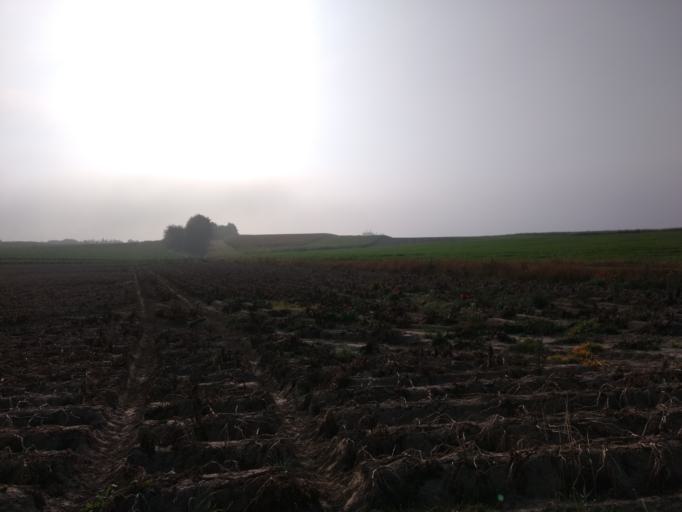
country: BE
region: Flanders
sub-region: Provincie Vlaams-Brabant
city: Herent
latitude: 50.8818
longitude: 4.6579
